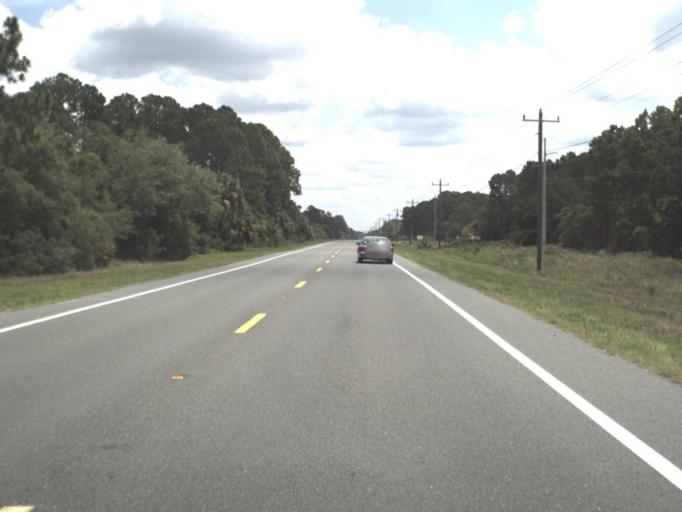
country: US
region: Florida
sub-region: Levy County
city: Chiefland
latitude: 29.1825
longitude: -83.0179
